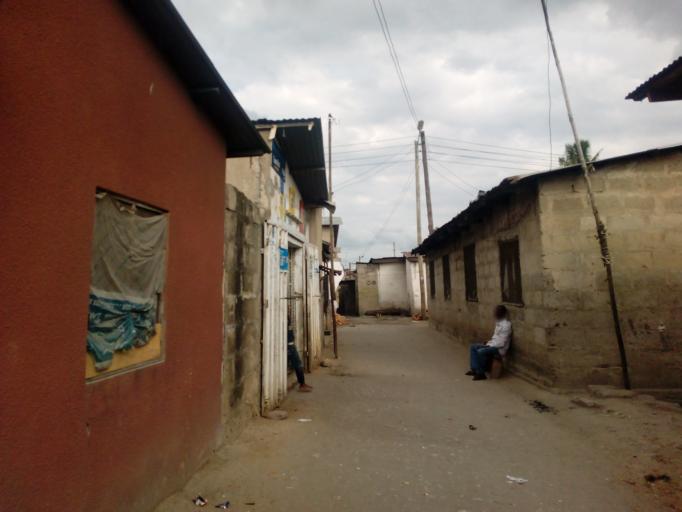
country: TZ
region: Dar es Salaam
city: Dar es Salaam
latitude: -6.8376
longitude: 39.2742
